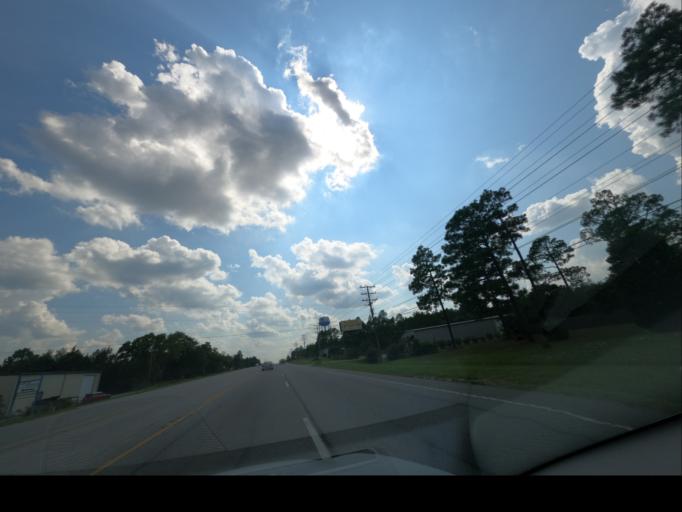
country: US
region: South Carolina
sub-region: Lexington County
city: South Congaree
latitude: 33.8925
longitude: -81.1587
